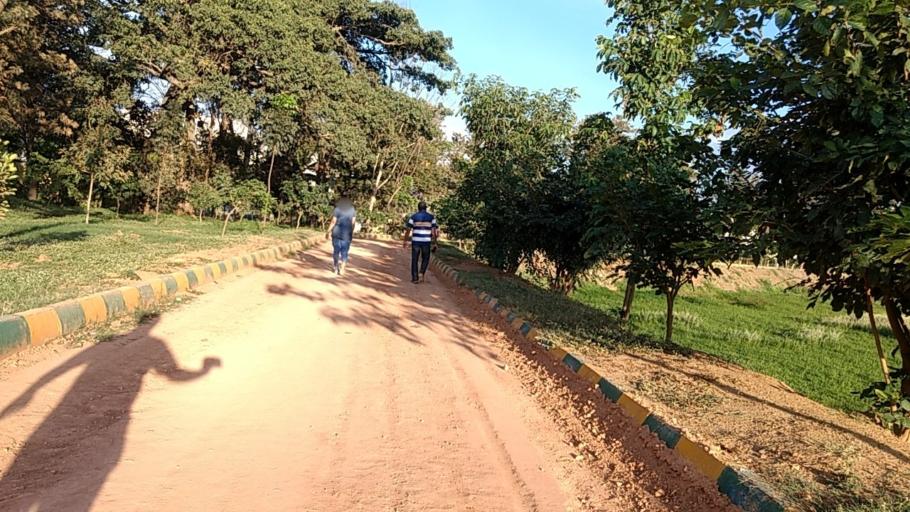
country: IN
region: Karnataka
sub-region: Bangalore Urban
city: Yelahanka
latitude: 13.0688
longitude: 77.5630
